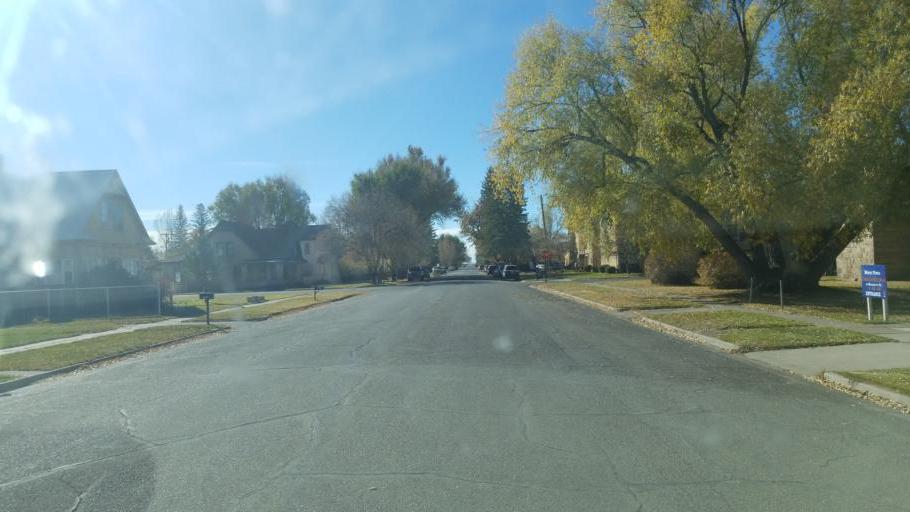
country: US
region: Colorado
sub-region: Rio Grande County
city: Monte Vista
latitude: 37.5785
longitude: -106.1481
